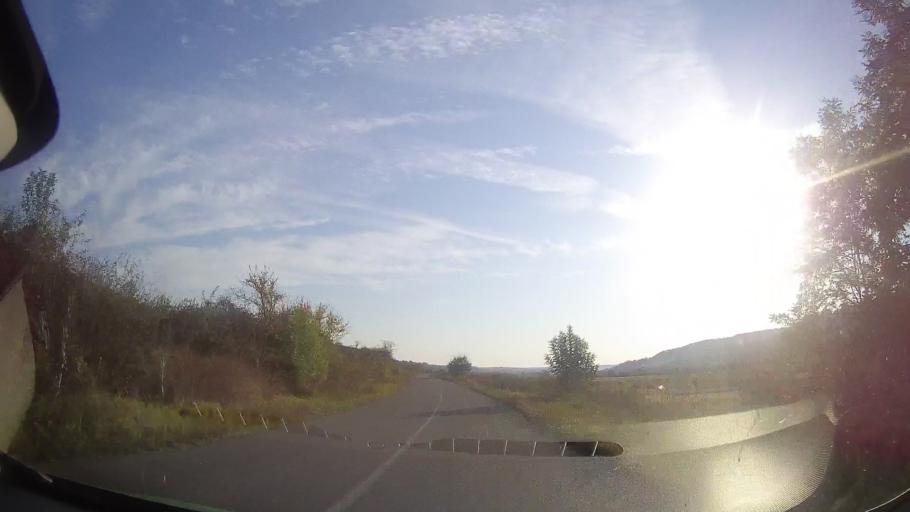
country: RO
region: Timis
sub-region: Comuna Bogda
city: Bogda
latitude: 45.9809
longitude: 21.5319
